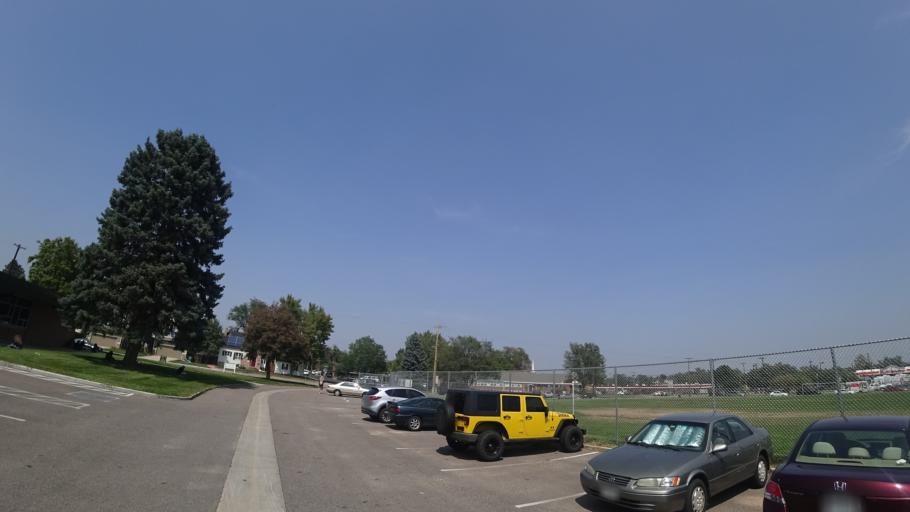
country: US
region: Colorado
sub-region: Arapahoe County
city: Englewood
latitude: 39.6271
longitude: -104.9905
